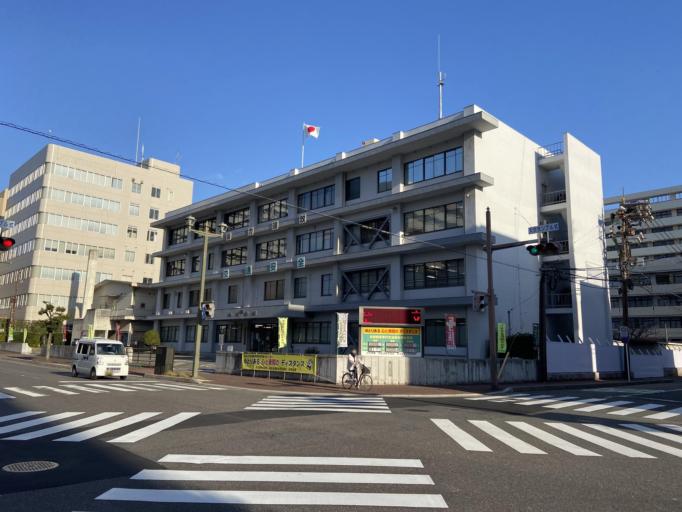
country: JP
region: Hiroshima
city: Kure
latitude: 34.2474
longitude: 132.5581
